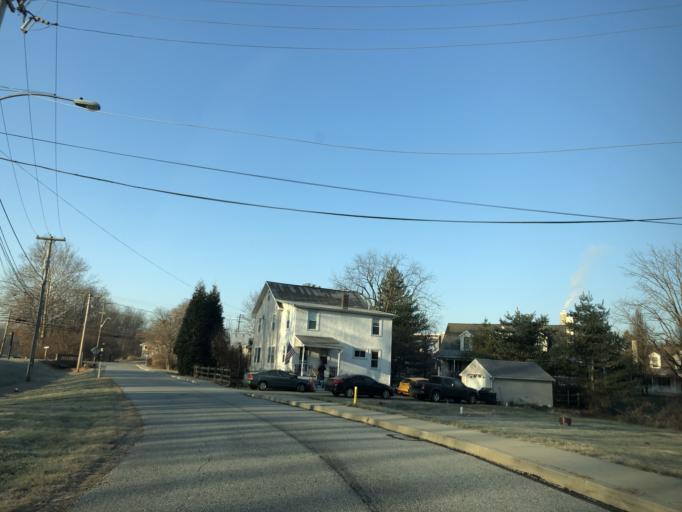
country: US
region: Pennsylvania
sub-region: Chester County
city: Downingtown
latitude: 40.0087
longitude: -75.7119
